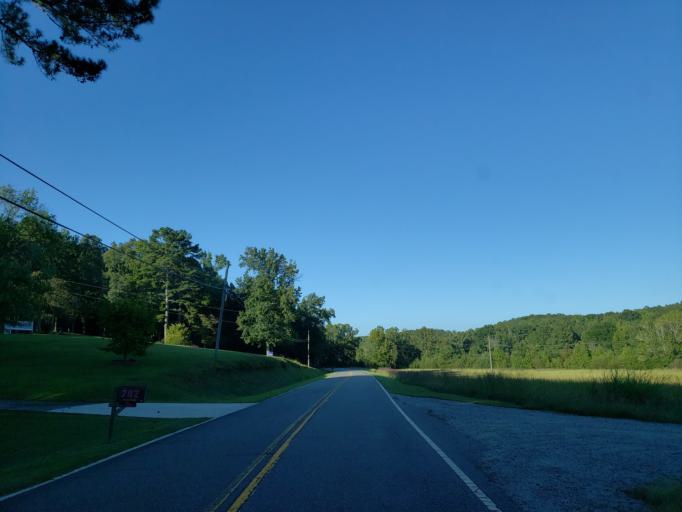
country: US
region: Georgia
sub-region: Bartow County
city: Rydal
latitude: 34.3083
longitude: -84.7591
